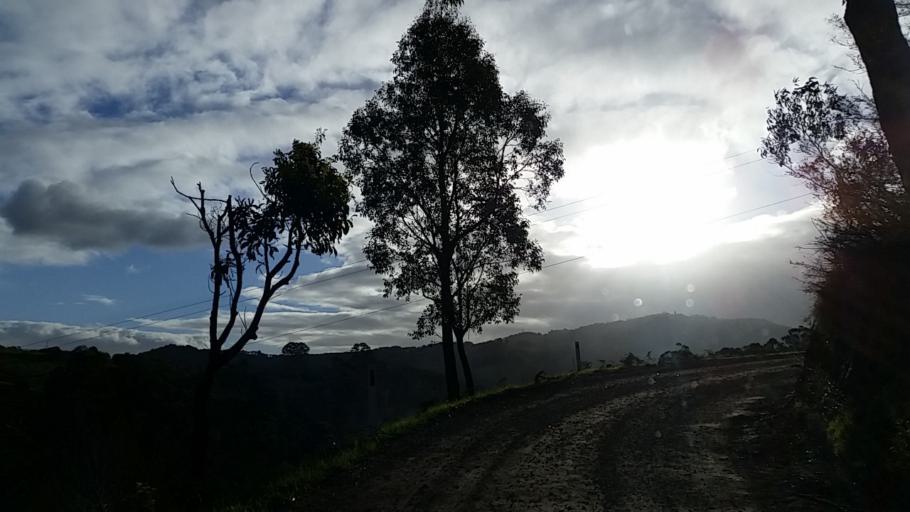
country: AU
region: South Australia
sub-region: Adelaide Hills
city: Balhannah
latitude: -34.9283
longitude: 138.7836
